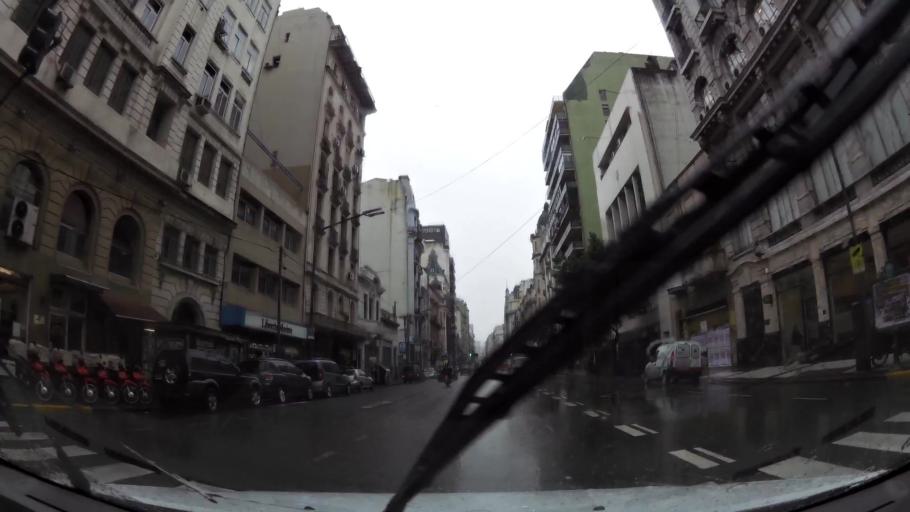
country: AR
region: Buenos Aires F.D.
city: Buenos Aires
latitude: -34.6067
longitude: -58.3922
